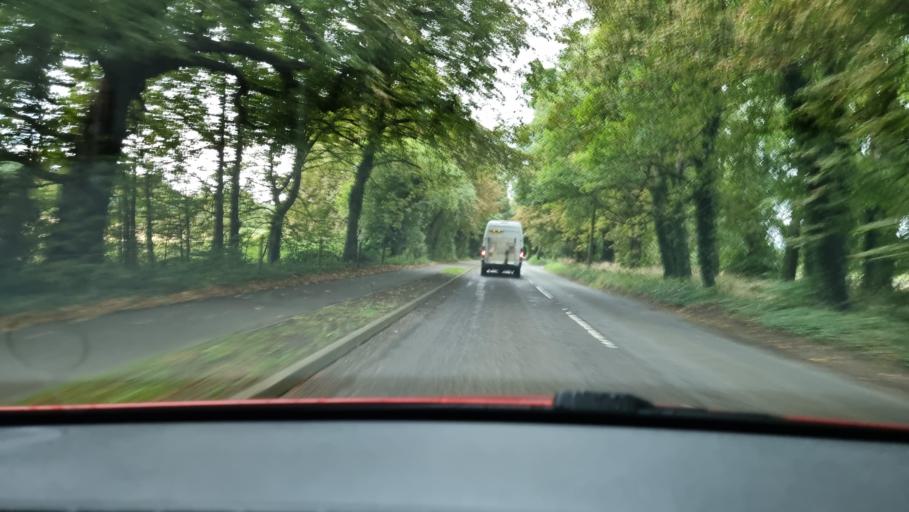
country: GB
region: England
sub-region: Hertfordshire
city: Tring
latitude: 51.7993
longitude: -0.6336
